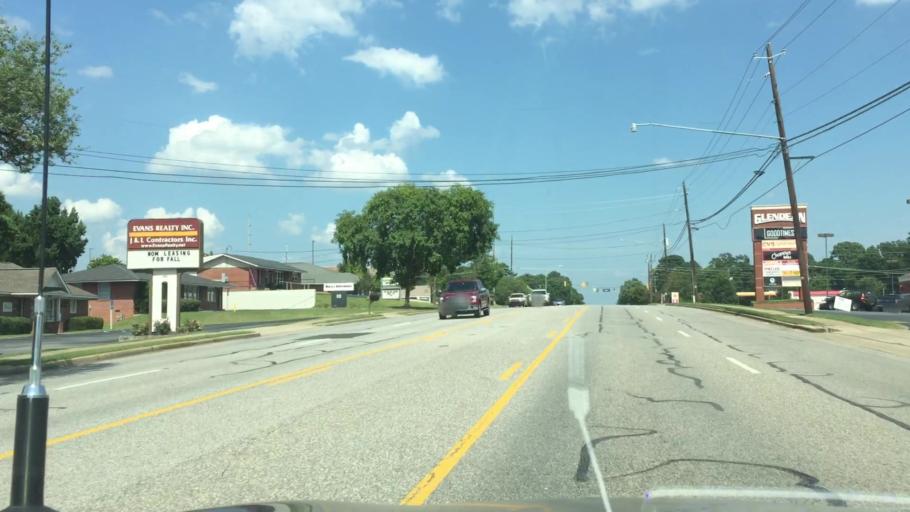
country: US
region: Alabama
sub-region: Lee County
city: Auburn
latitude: 32.6090
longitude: -85.4674
